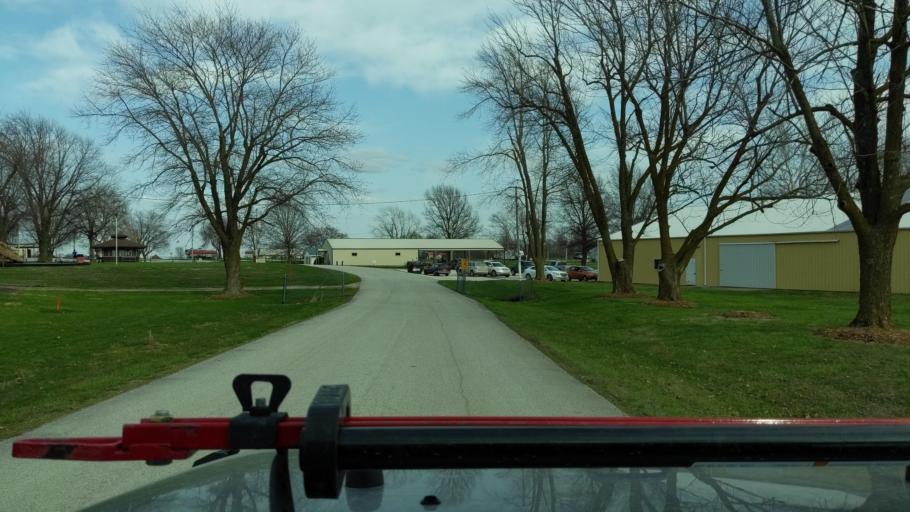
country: US
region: Missouri
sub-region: Macon County
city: Macon
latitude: 39.7210
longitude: -92.4630
